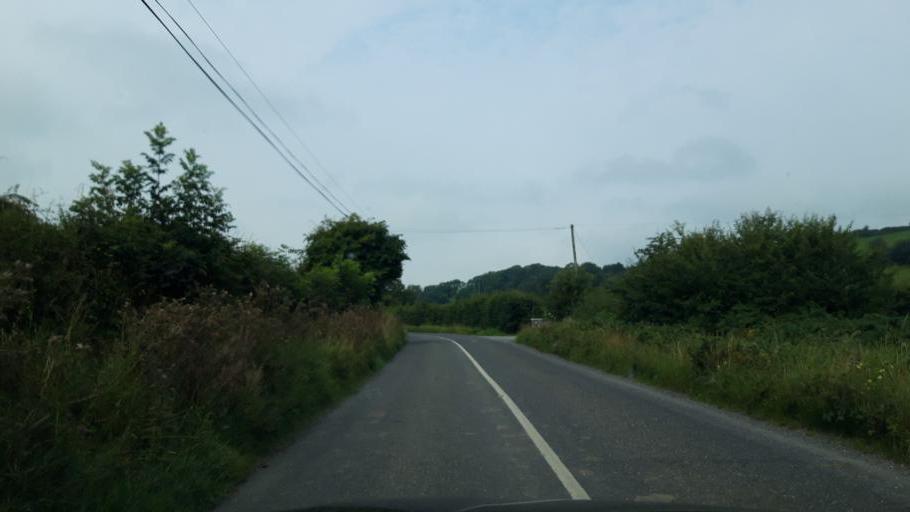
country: IE
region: Munster
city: Fethard
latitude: 52.5829
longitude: -7.6124
